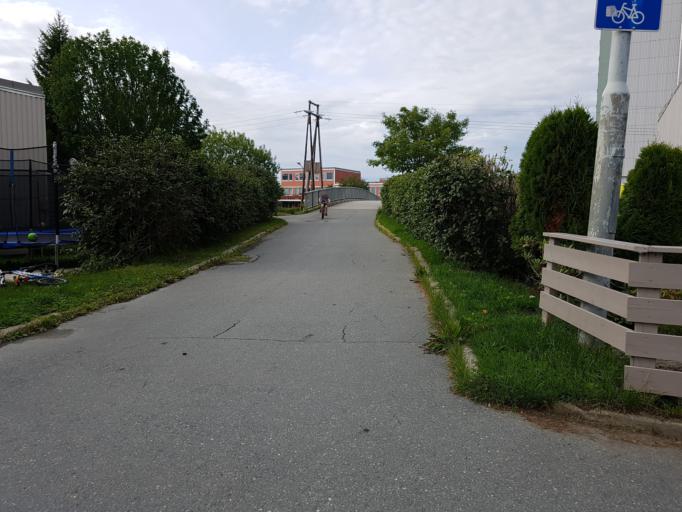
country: NO
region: Sor-Trondelag
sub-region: Trondheim
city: Trondheim
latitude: 63.3902
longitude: 10.4302
